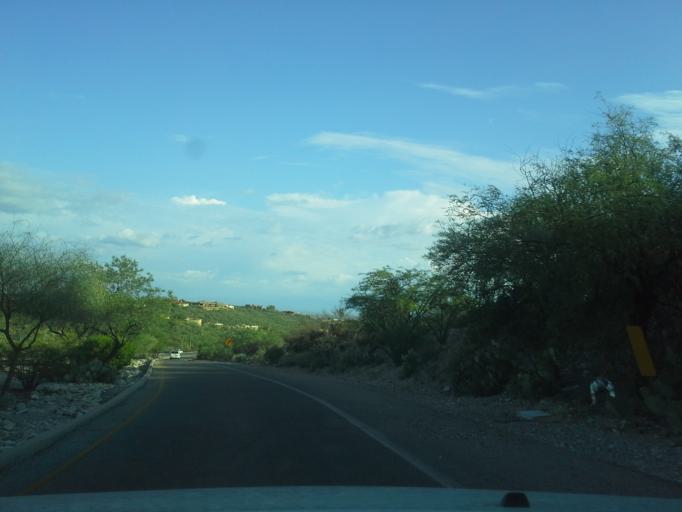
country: US
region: Arizona
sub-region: Pima County
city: Catalina Foothills
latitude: 32.3271
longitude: -110.8706
